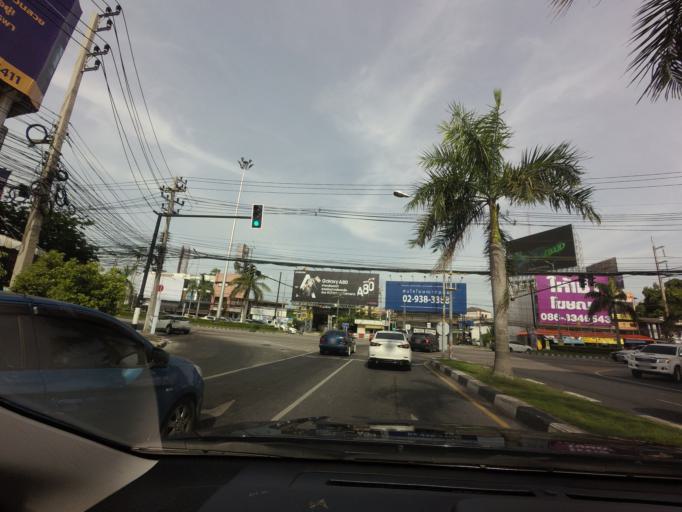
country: TH
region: Chon Buri
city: Chon Buri
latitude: 13.2866
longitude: 100.9389
